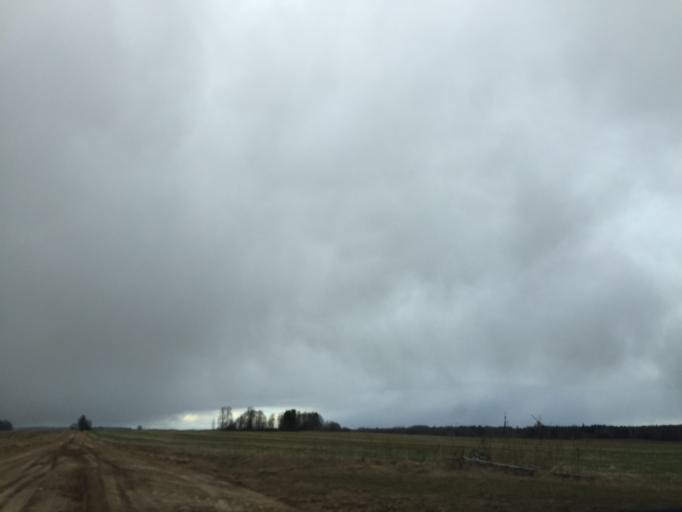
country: LV
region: Akniste
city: Akniste
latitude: 56.0662
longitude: 25.8057
